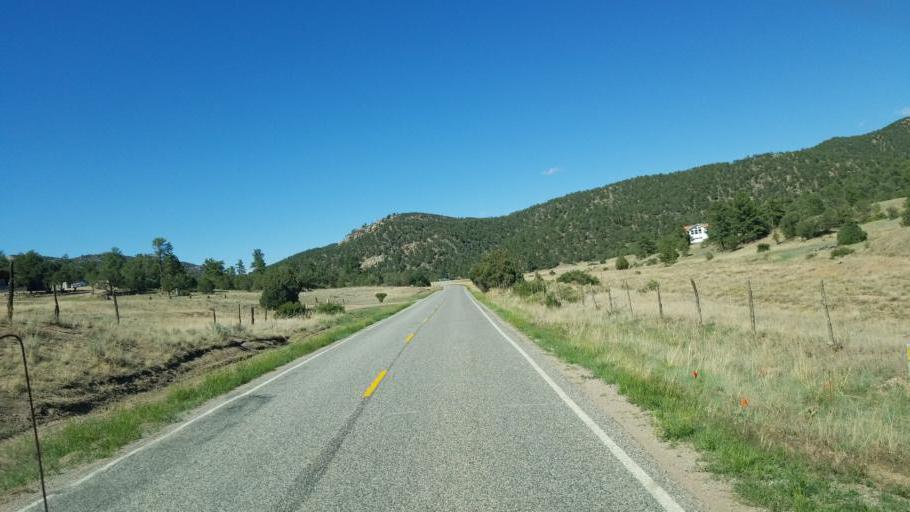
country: US
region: Colorado
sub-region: Fremont County
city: Canon City
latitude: 38.3696
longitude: -105.4595
